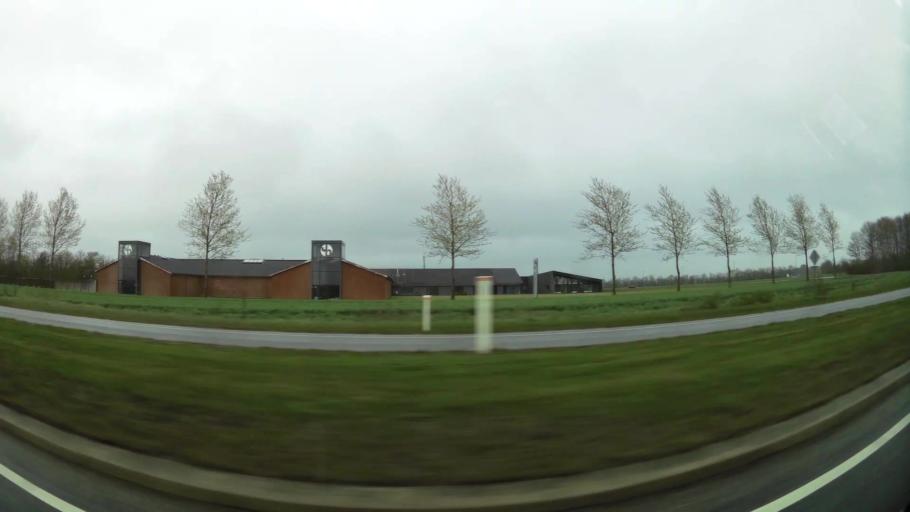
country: DK
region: Central Jutland
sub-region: Herning Kommune
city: Avlum
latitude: 56.2493
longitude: 8.7961
